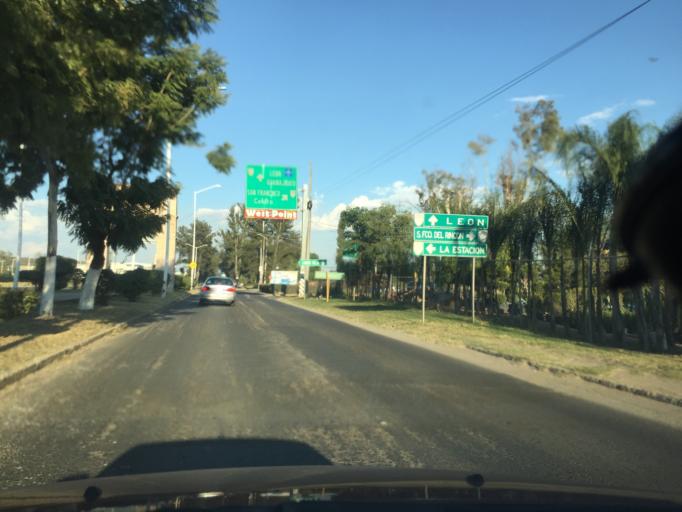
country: MX
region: Guanajuato
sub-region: San Francisco del Rincon
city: Estacion de San Francisco
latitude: 21.0321
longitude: -101.8300
